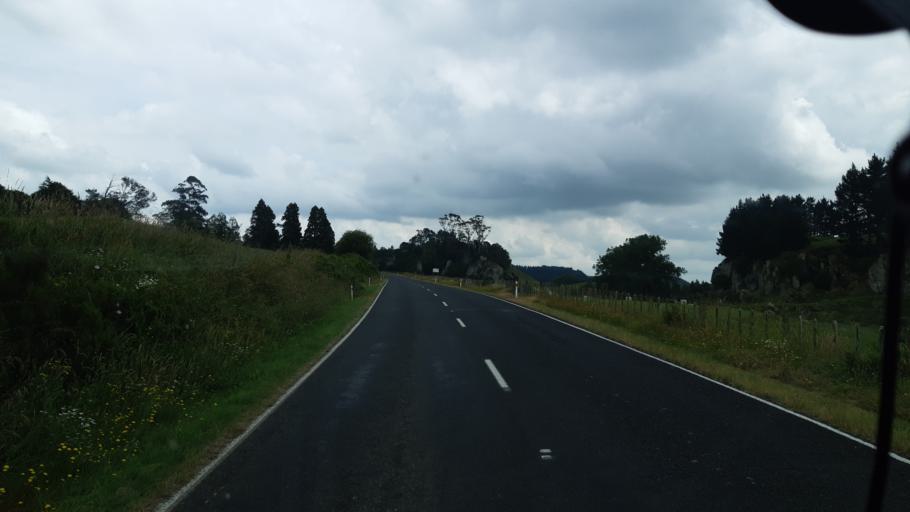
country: NZ
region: Waikato
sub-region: Waipa District
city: Cambridge
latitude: -38.1333
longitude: 175.5281
